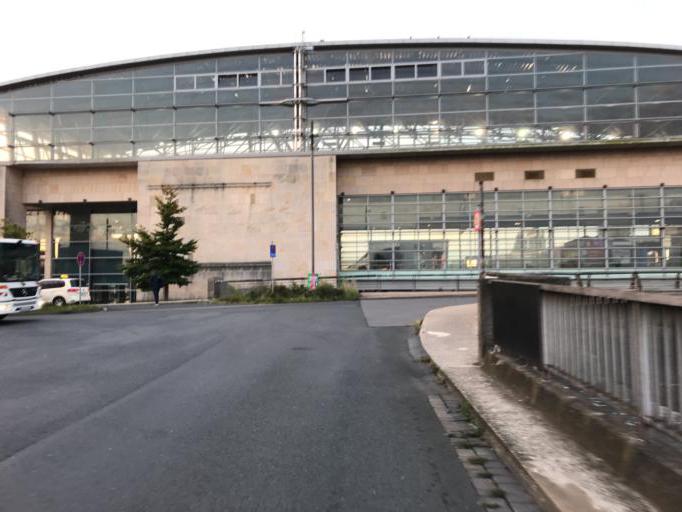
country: DE
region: Lower Saxony
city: Laatzen
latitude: 52.3180
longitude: 9.7925
